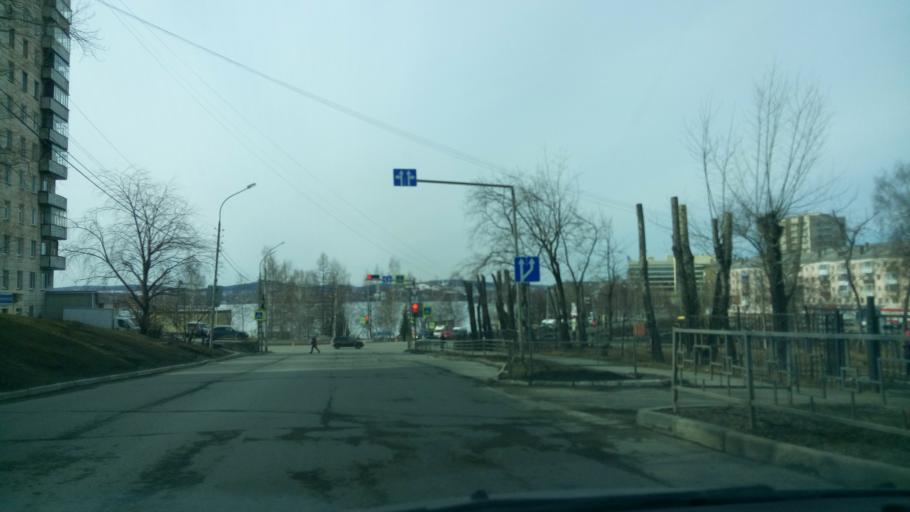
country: RU
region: Sverdlovsk
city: Nizhniy Tagil
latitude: 57.9048
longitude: 59.9916
